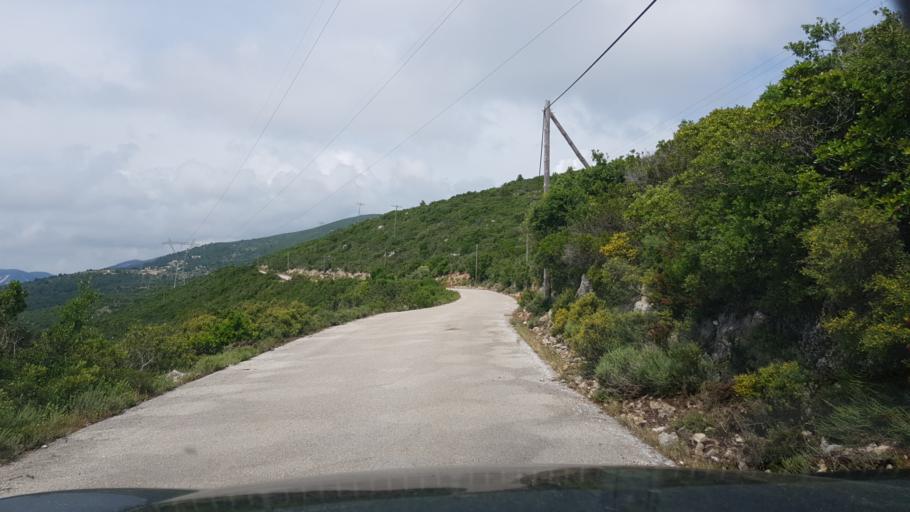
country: GR
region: Ionian Islands
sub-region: Lefkada
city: Nidri
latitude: 38.6035
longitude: 20.5597
